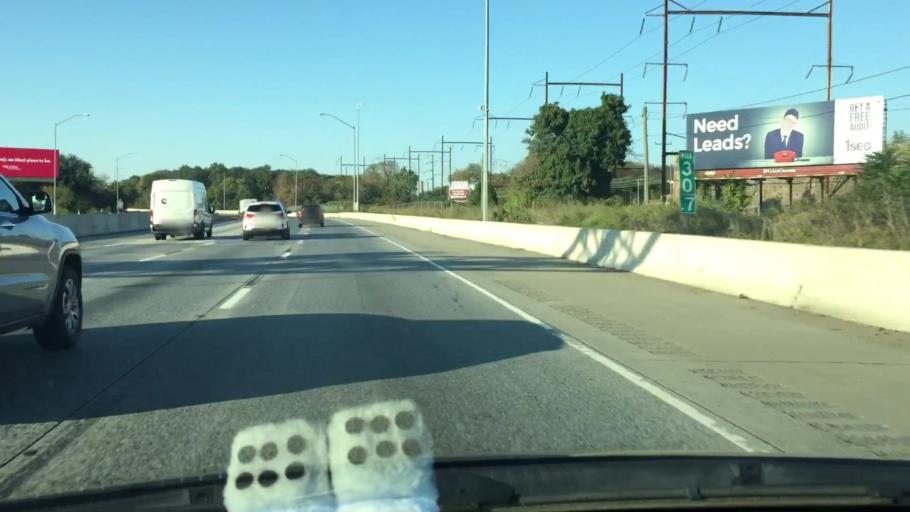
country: US
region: New Jersey
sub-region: Burlington County
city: Riverton
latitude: 40.0362
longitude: -75.0175
